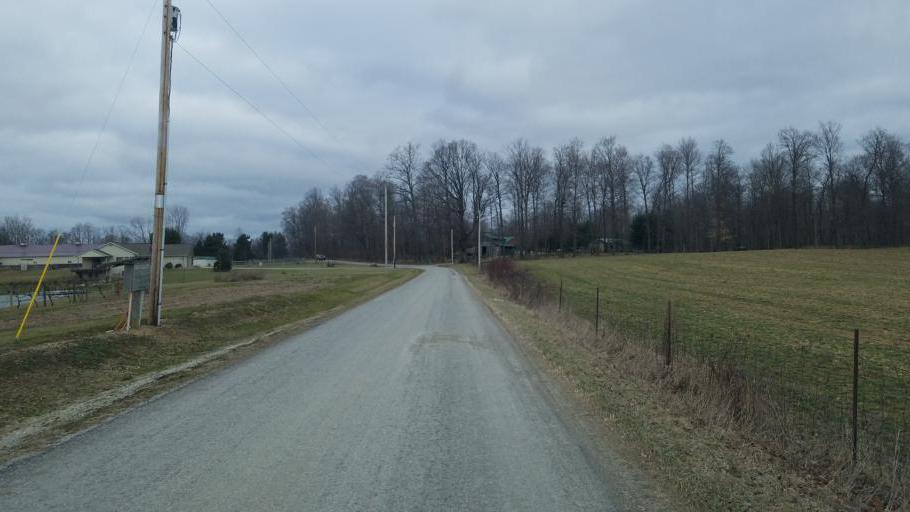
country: US
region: Ohio
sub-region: Morrow County
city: Mount Gilead
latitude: 40.5692
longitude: -82.6970
